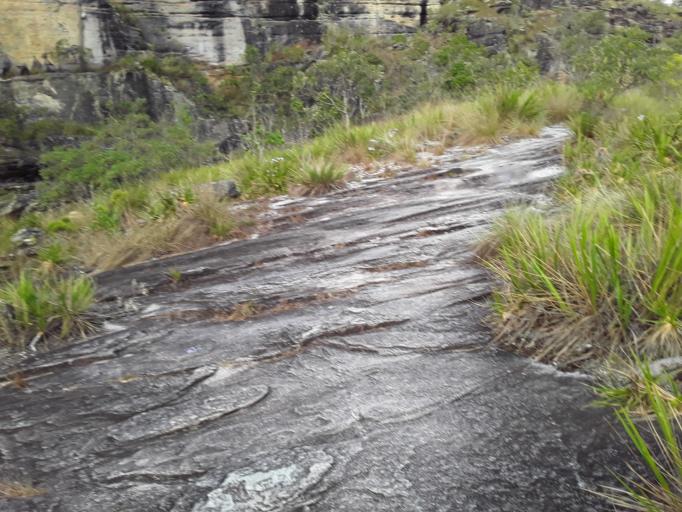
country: BR
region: Minas Gerais
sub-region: Lima Duarte
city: Lima Duarte
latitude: -21.7113
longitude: -43.8939
